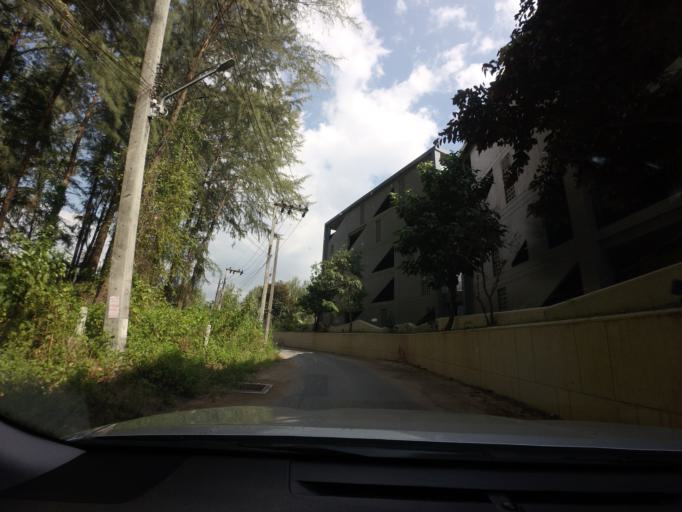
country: TH
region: Phangnga
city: Ban Khao Lak
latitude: 8.6617
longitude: 98.2477
